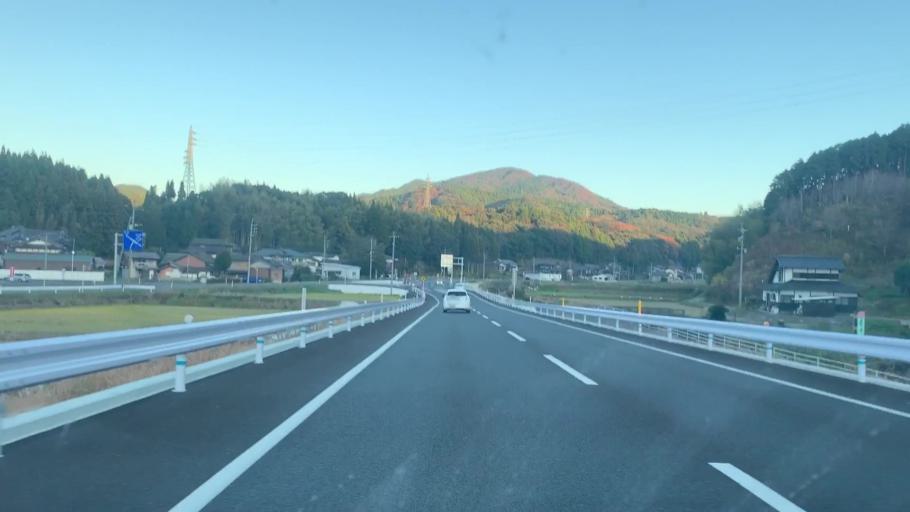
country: JP
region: Saga Prefecture
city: Takeocho-takeo
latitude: 33.2500
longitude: 129.9972
